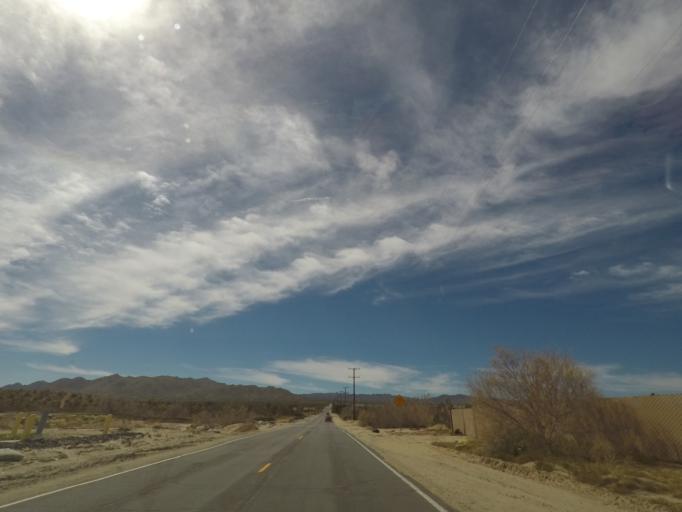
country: US
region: California
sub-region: San Bernardino County
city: Joshua Tree
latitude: 34.1413
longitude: -116.3696
